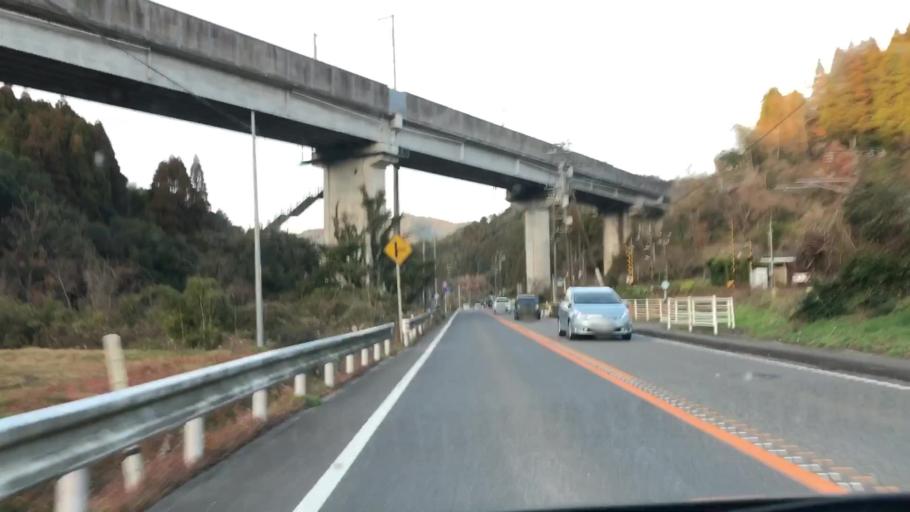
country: JP
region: Kumamoto
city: Minamata
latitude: 32.2171
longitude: 130.4375
